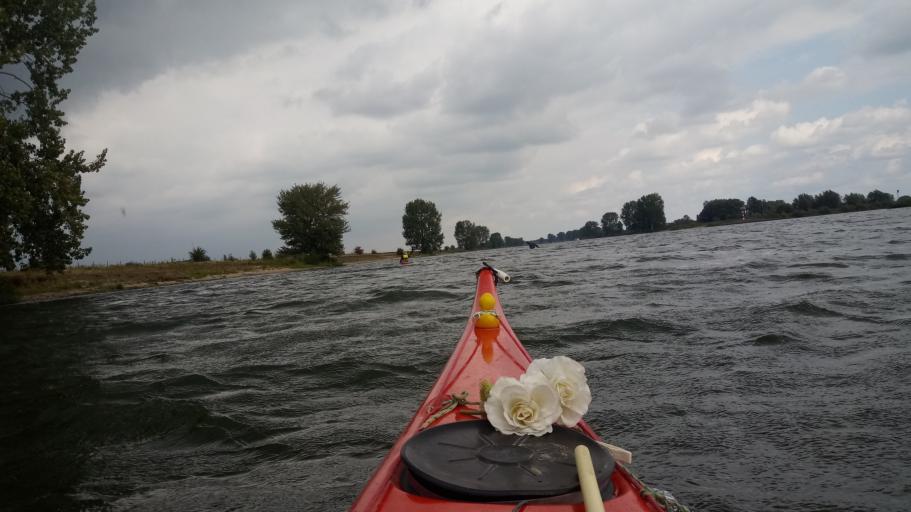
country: NL
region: North Brabant
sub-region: Gemeente 's-Hertogenbosch
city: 's-Hertogenbosch
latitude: 51.7472
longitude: 5.3224
